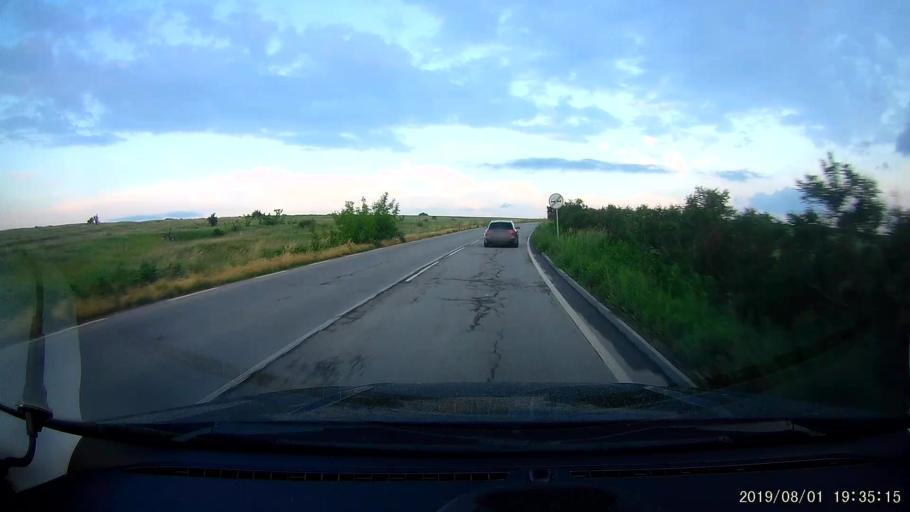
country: BG
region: Burgas
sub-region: Obshtina Sungurlare
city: Sungurlare
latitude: 42.7627
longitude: 26.8837
